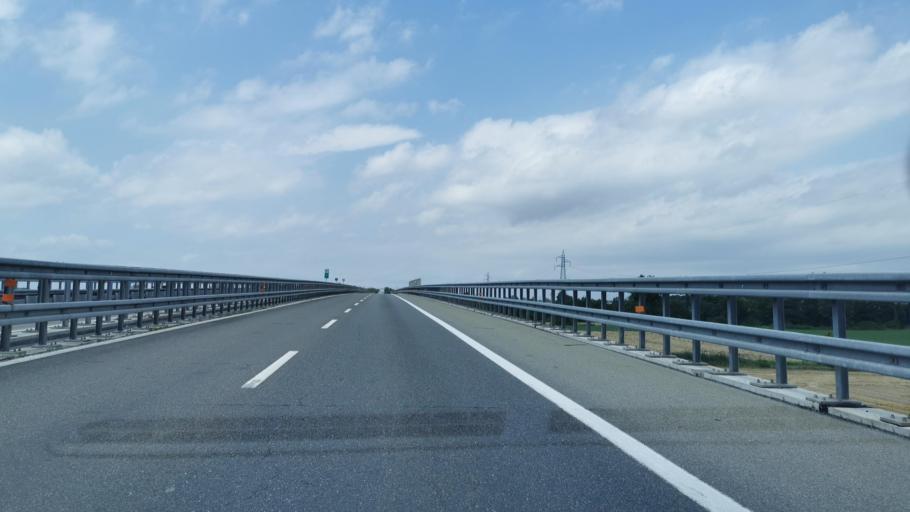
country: IT
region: Piedmont
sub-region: Provincia di Alessandria
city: Alessandria
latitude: 44.9420
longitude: 8.5975
